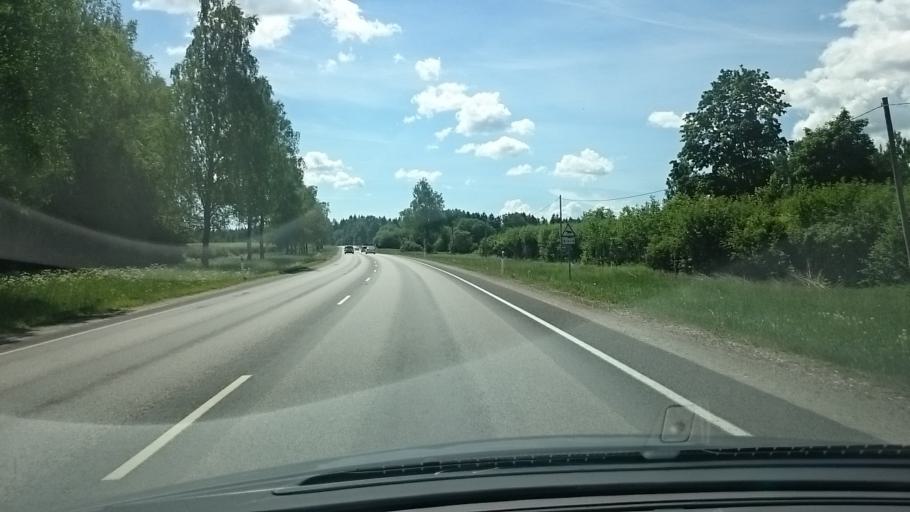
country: EE
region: Jaervamaa
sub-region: Paide linn
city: Paide
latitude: 58.9897
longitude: 25.5918
